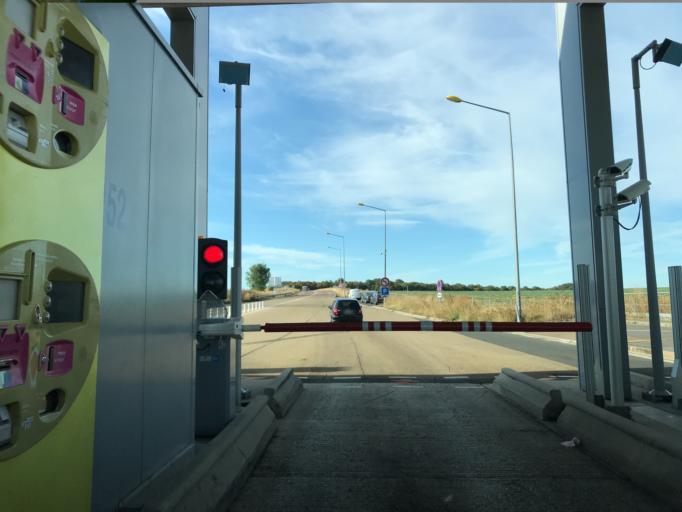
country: FR
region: Champagne-Ardenne
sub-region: Departement de la Marne
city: Chatillon-sur-Marne
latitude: 49.1538
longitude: 3.7169
